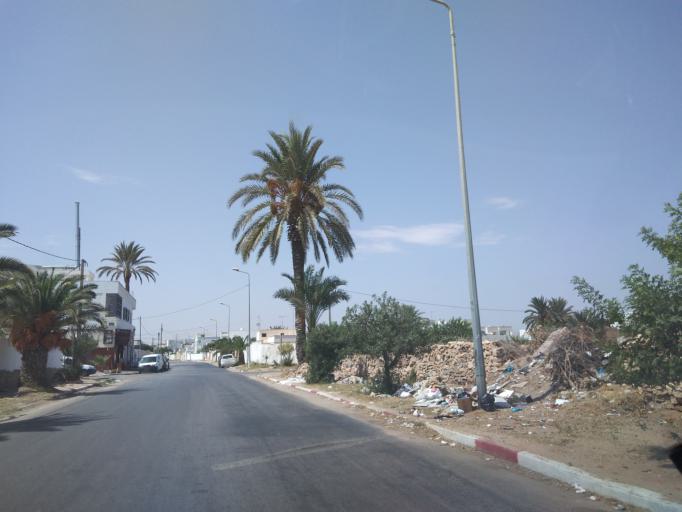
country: TN
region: Safaqis
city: Sfax
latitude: 34.7561
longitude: 10.7530
